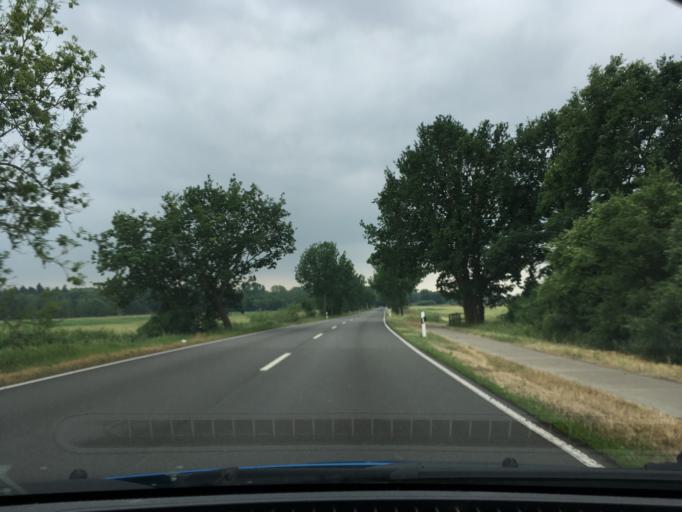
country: DE
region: Lower Saxony
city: Lubbow
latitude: 52.8992
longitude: 11.1797
